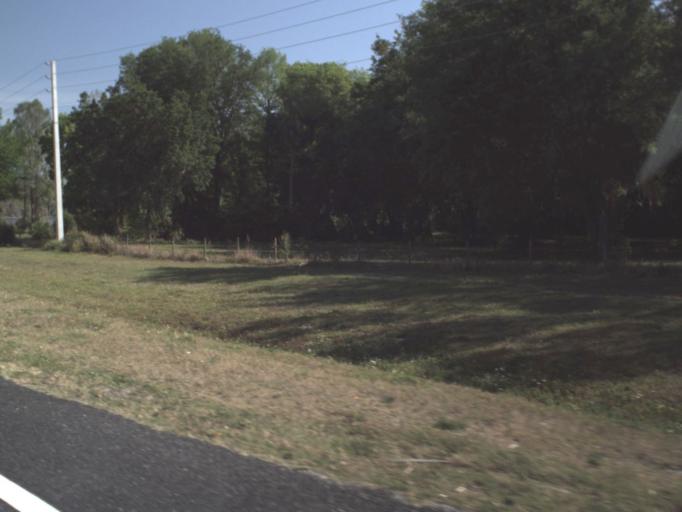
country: US
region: Florida
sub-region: Lake County
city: Hawthorne
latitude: 28.7810
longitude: -81.8877
